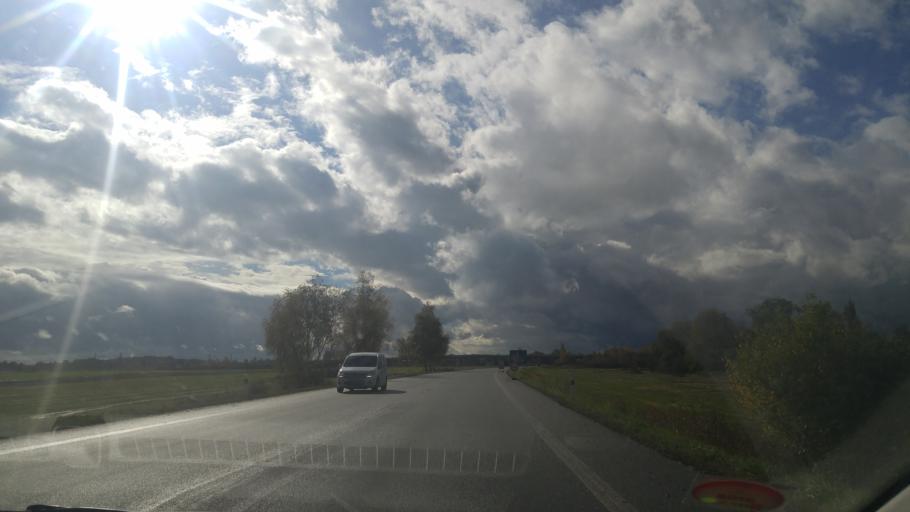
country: CZ
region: Jihocesky
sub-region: Okres Tabor
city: Veseli nad Luznici
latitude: 49.1760
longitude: 14.6867
